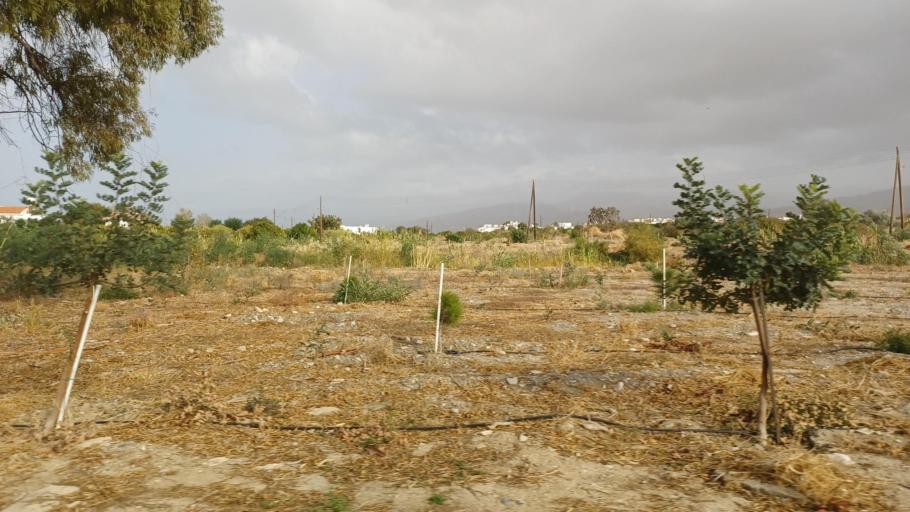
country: CY
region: Pafos
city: Polis
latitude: 35.0417
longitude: 32.4228
